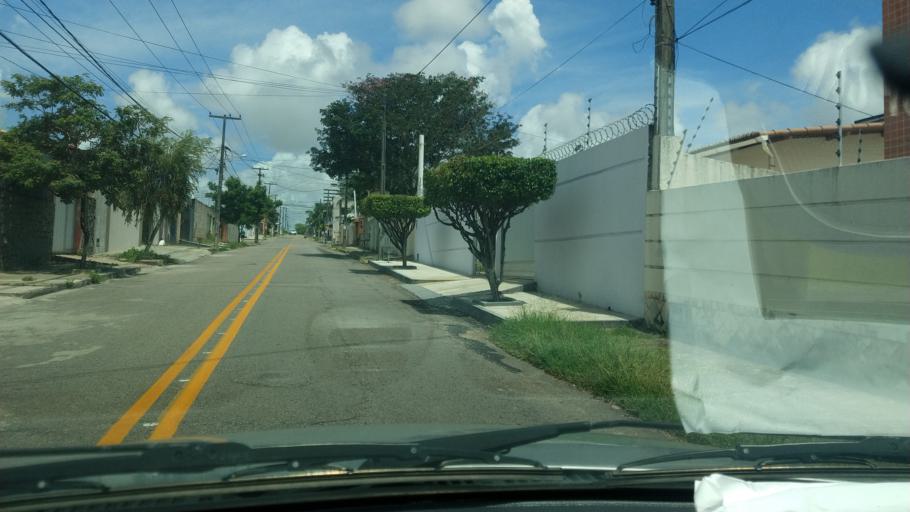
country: BR
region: Rio Grande do Norte
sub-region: Natal
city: Natal
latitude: -5.8666
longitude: -35.1976
